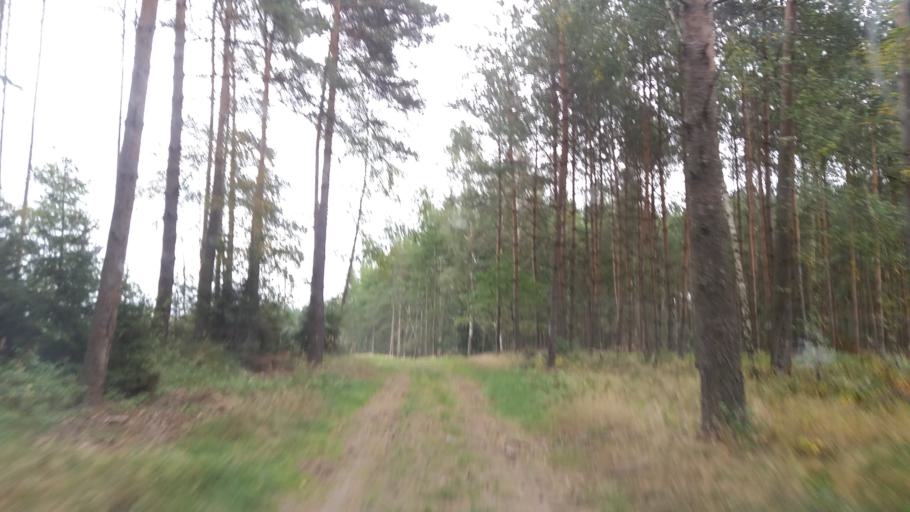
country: PL
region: West Pomeranian Voivodeship
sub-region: Powiat choszczenski
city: Bierzwnik
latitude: 52.9885
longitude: 15.5972
